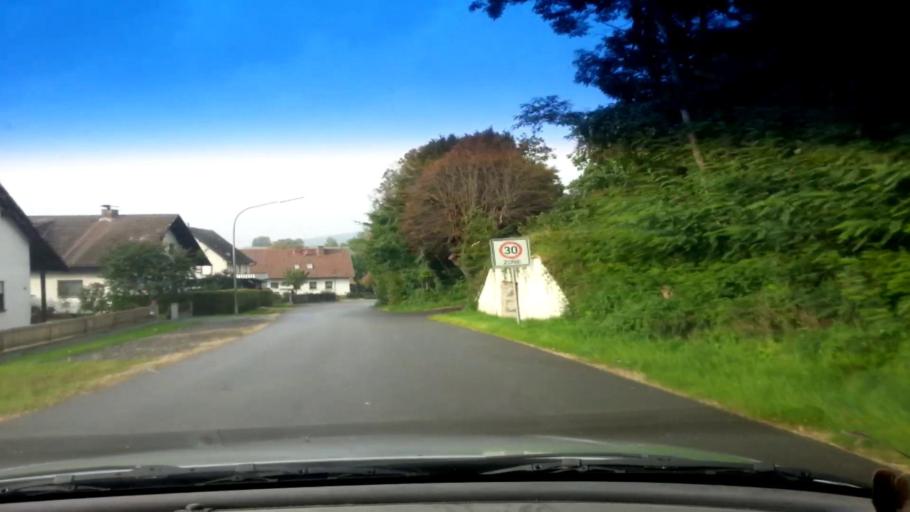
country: DE
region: Bavaria
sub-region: Upper Franconia
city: Rattelsdorf
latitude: 50.0462
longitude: 10.8834
